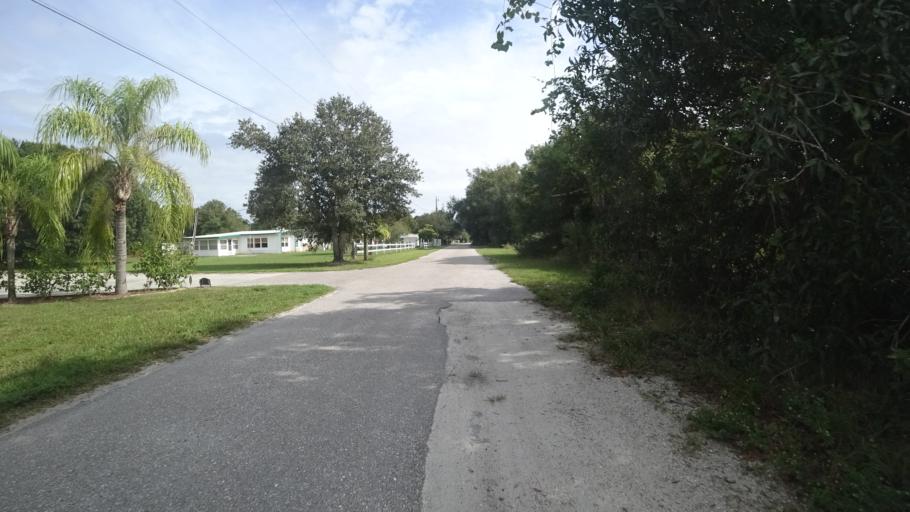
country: US
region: Florida
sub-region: Sarasota County
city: North Sarasota
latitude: 27.3870
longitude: -82.5154
